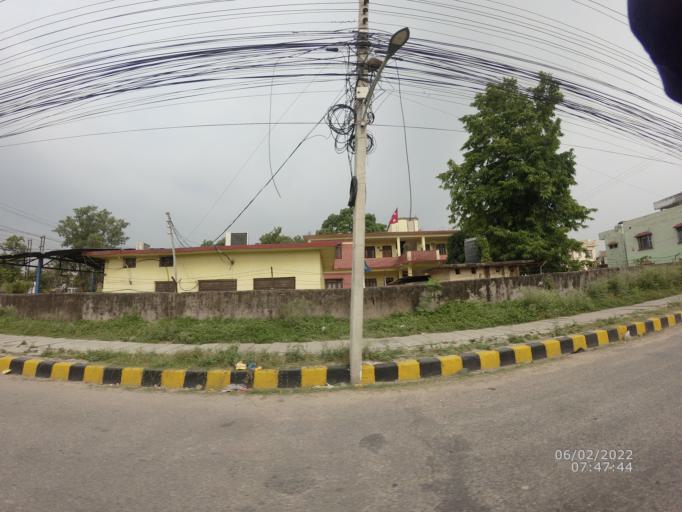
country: NP
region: Western Region
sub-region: Lumbini Zone
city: Bhairahawa
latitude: 27.5224
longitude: 83.4547
